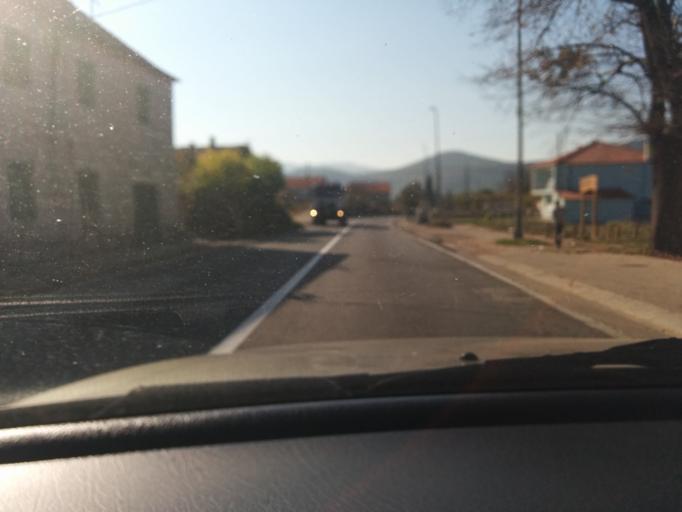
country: HR
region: Splitsko-Dalmatinska
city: Dugopolje
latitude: 43.6383
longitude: 16.5968
